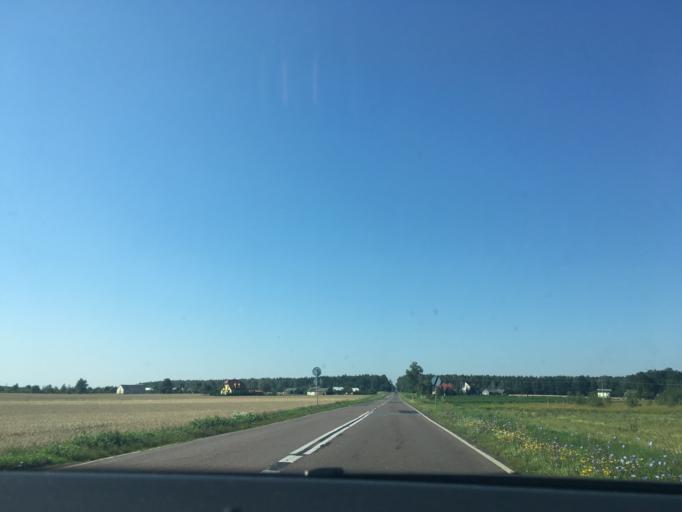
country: PL
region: Lublin Voivodeship
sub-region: Powiat radzynski
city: Borki
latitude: 51.7138
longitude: 22.5236
